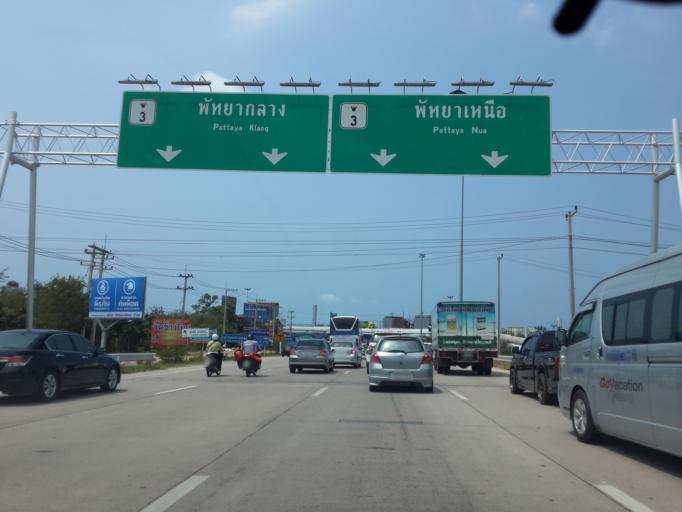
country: TH
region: Chon Buri
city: Phatthaya
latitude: 12.9445
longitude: 100.9073
